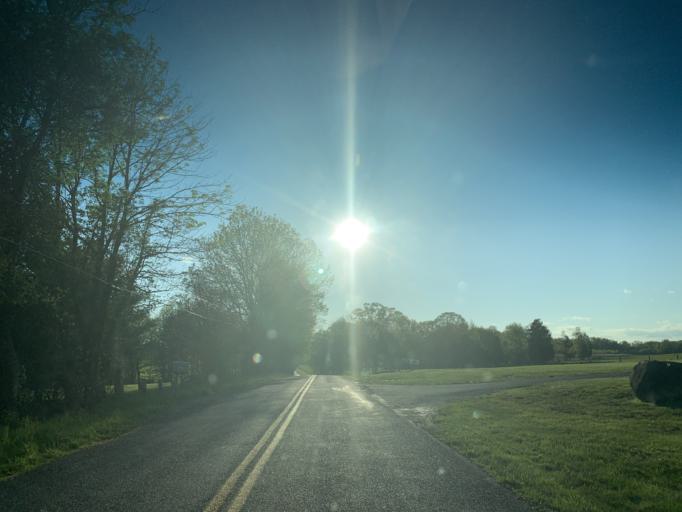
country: US
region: Maryland
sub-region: Harford County
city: Aberdeen
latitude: 39.5504
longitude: -76.1850
